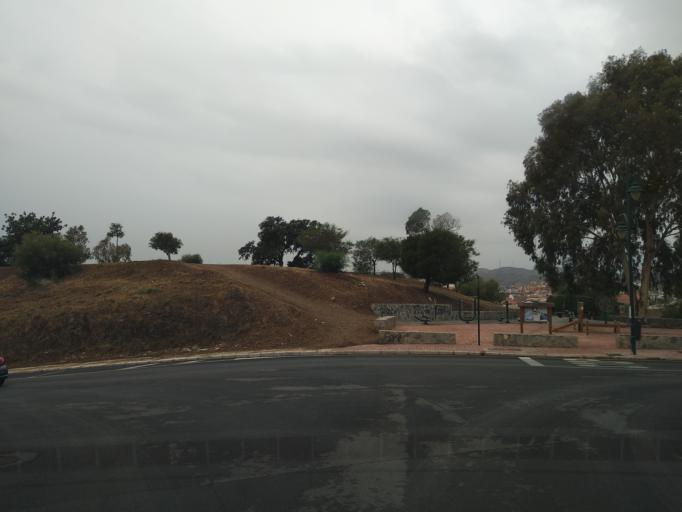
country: ES
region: Andalusia
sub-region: Provincia de Malaga
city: Malaga
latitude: 36.7422
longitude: -4.4768
